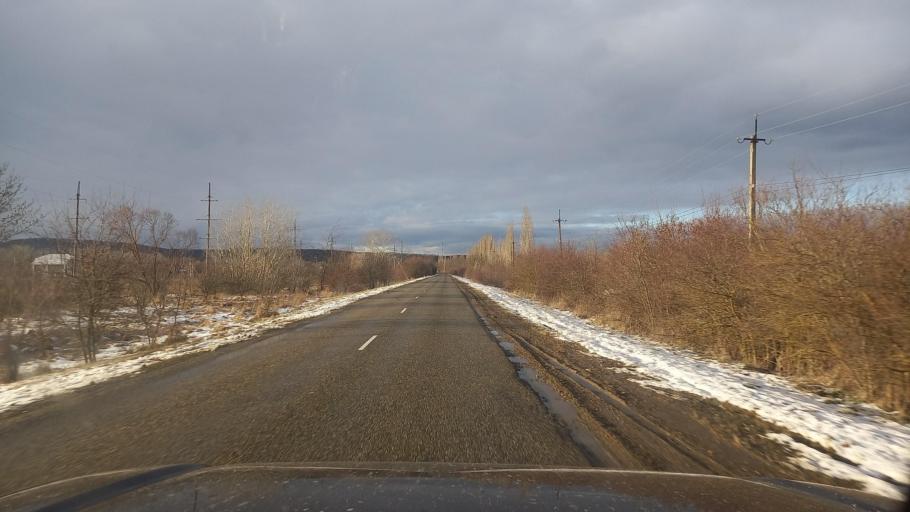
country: RU
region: Krasnodarskiy
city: Smolenskaya
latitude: 44.7757
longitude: 38.8146
